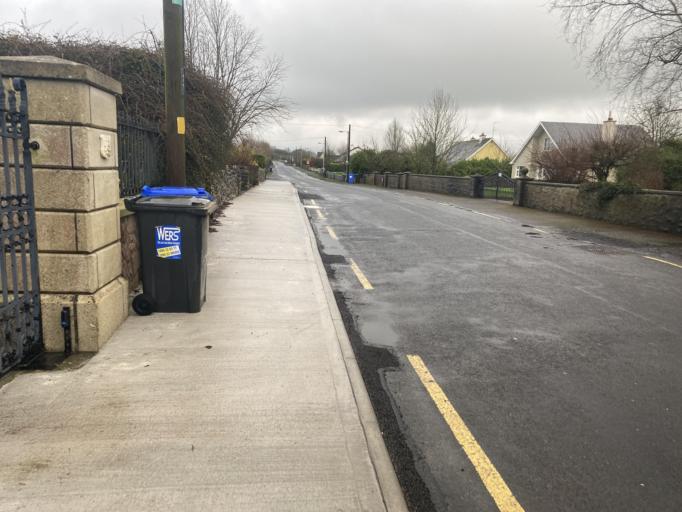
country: IE
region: Connaught
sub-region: County Galway
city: Tuam
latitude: 53.5213
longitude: -8.8300
